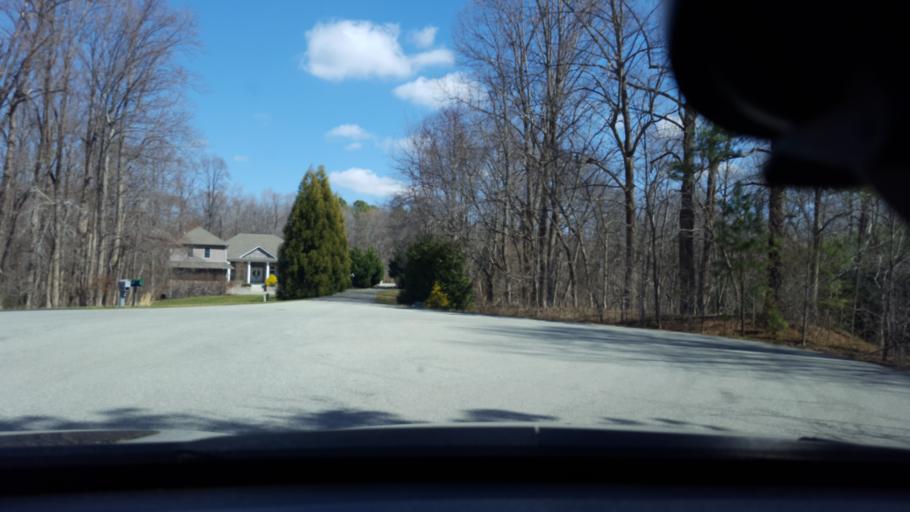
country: US
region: Maryland
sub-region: Calvert County
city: Chesapeake Beach
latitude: 38.6322
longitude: -76.5264
